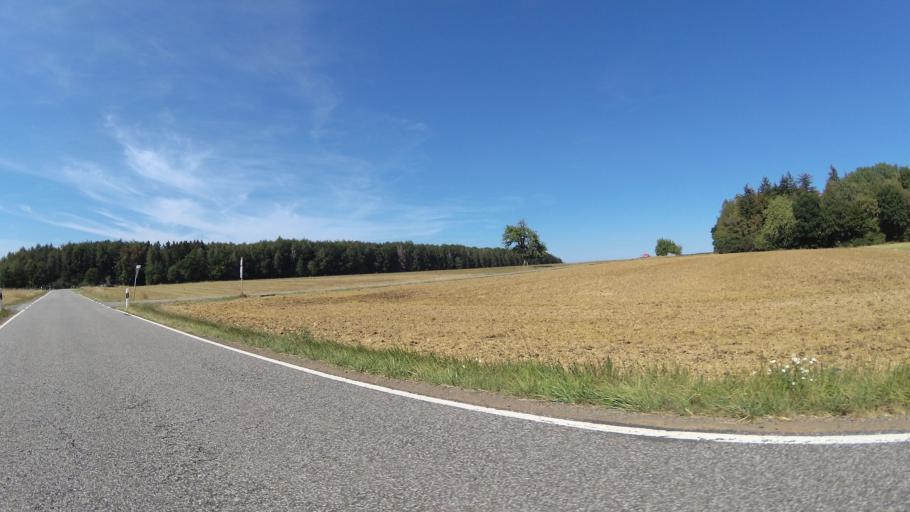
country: DE
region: Rheinland-Pfalz
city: Hornbach
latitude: 49.1592
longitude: 7.3218
